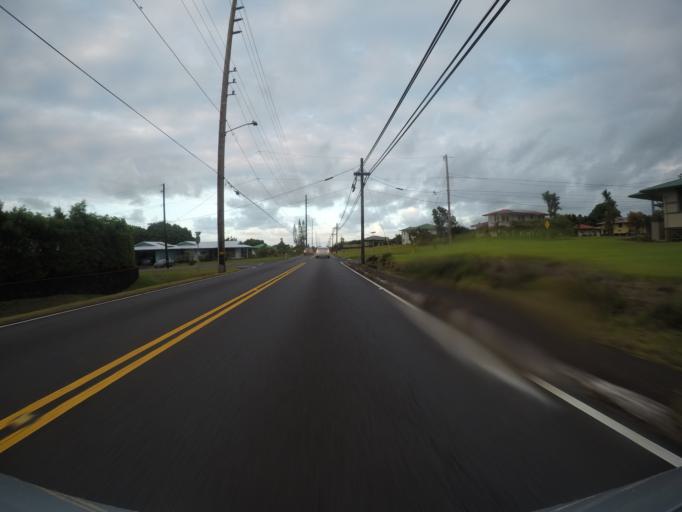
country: US
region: Hawaii
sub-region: Hawaii County
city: Hilo
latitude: 19.6841
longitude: -155.0765
